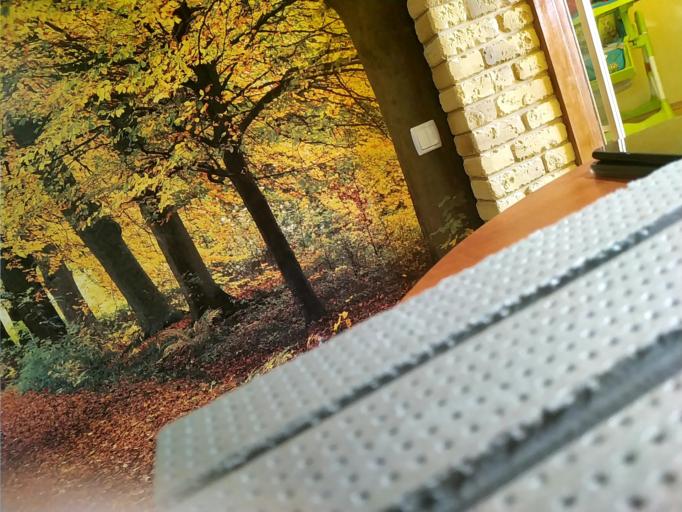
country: RU
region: Vologda
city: Nelazskoye
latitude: 59.4901
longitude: 37.6046
